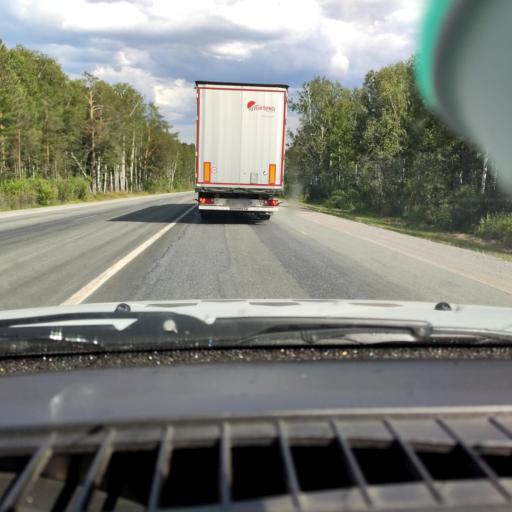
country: RU
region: Chelyabinsk
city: Syrostan
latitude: 55.0154
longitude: 59.7894
